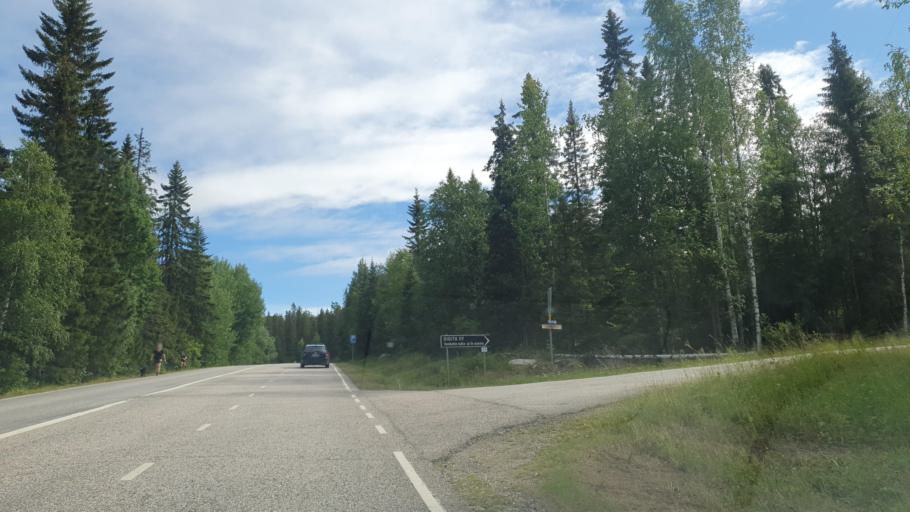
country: FI
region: Kainuu
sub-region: Kajaani
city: Vuokatti
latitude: 64.1297
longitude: 28.2538
